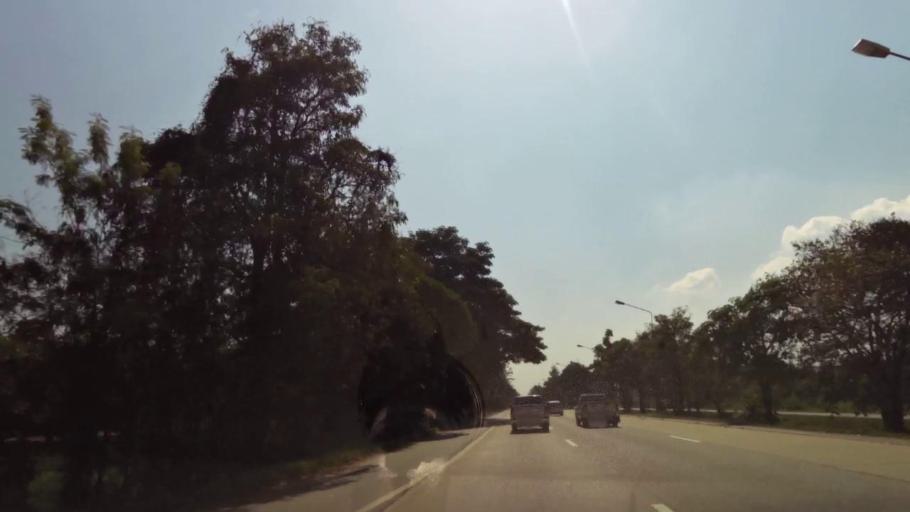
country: TH
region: Phichit
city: Wachira Barami
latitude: 16.5738
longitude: 100.1484
